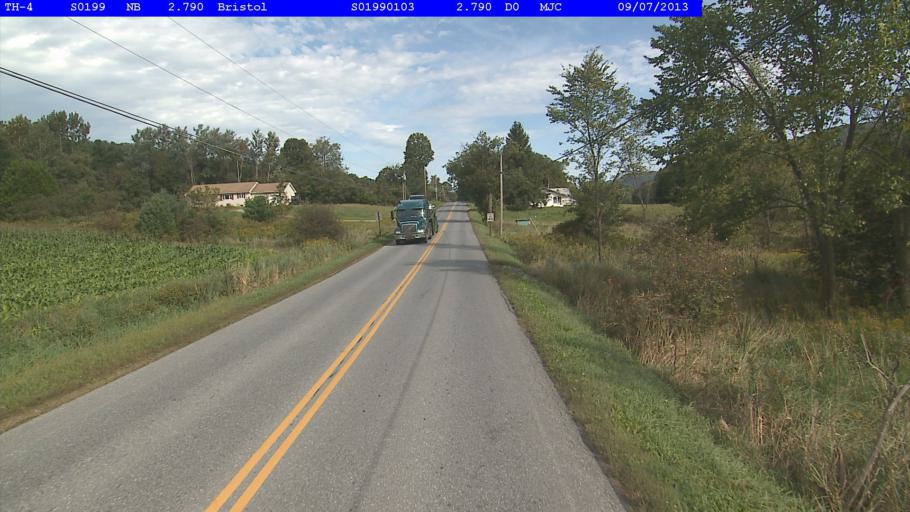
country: US
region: Vermont
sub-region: Addison County
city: Bristol
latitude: 44.1683
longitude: -73.1010
